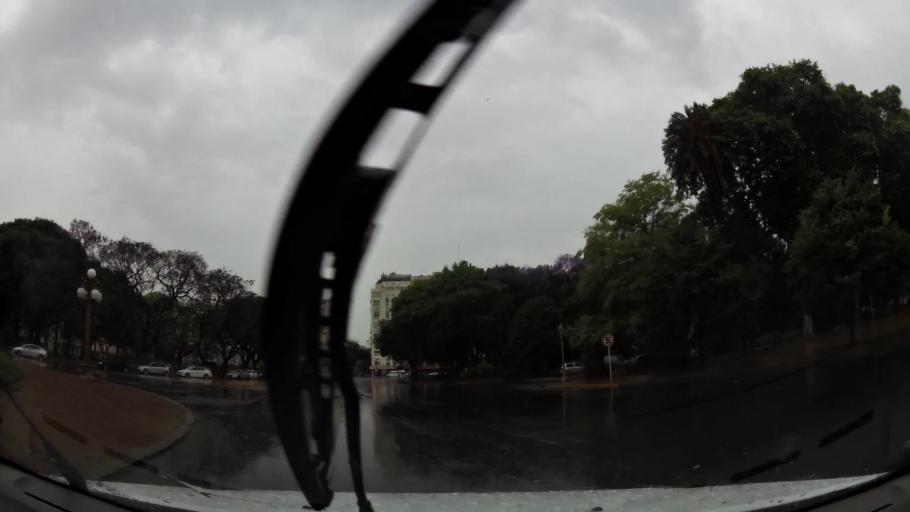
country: AR
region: Buenos Aires F.D.
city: Retiro
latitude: -34.5806
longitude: -58.4012
